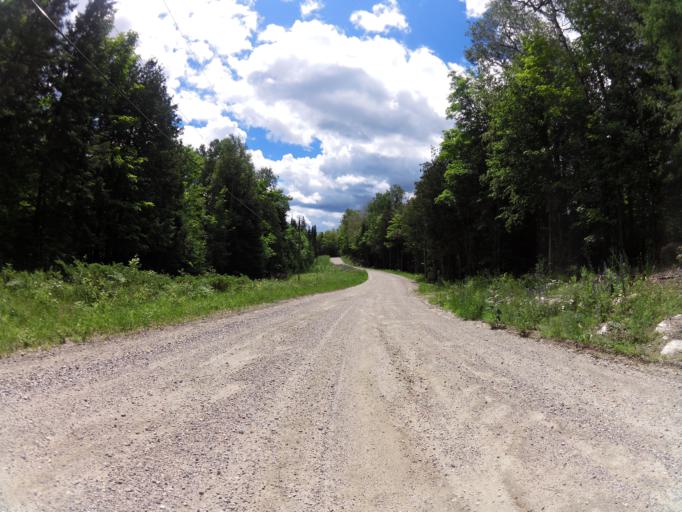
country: CA
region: Ontario
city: Renfrew
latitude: 45.0323
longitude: -76.7452
